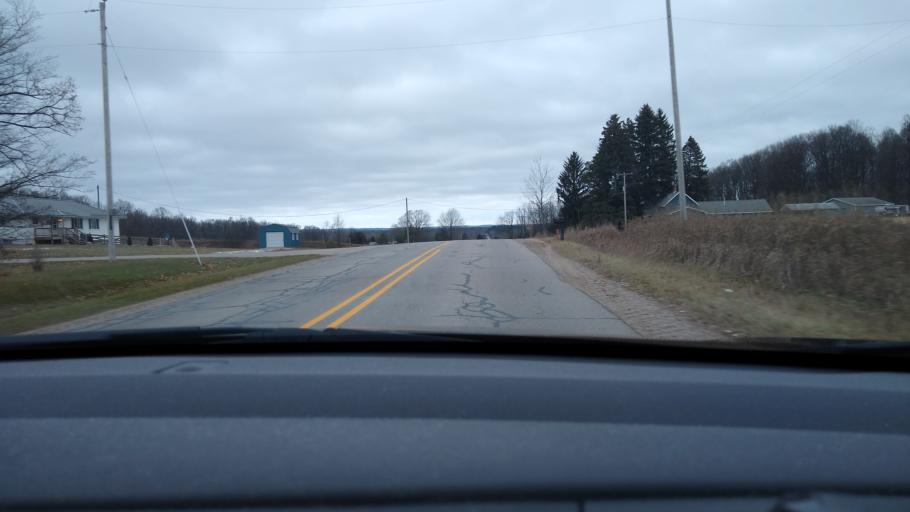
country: US
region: Michigan
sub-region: Missaukee County
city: Lake City
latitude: 44.3271
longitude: -85.0549
